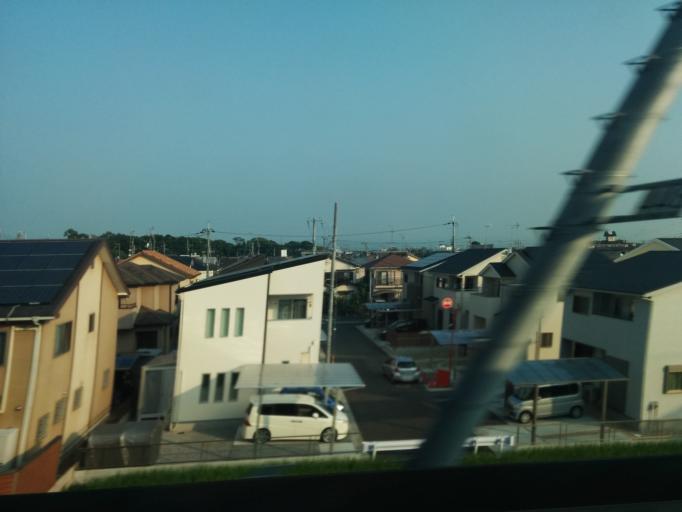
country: JP
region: Shiga Prefecture
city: Moriyama
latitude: 35.0581
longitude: 136.0184
